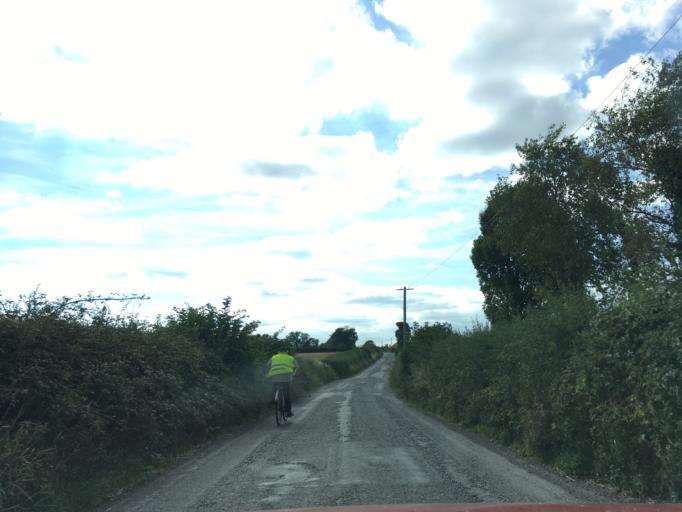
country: IE
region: Munster
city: Cashel
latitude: 52.4791
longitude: -7.9156
